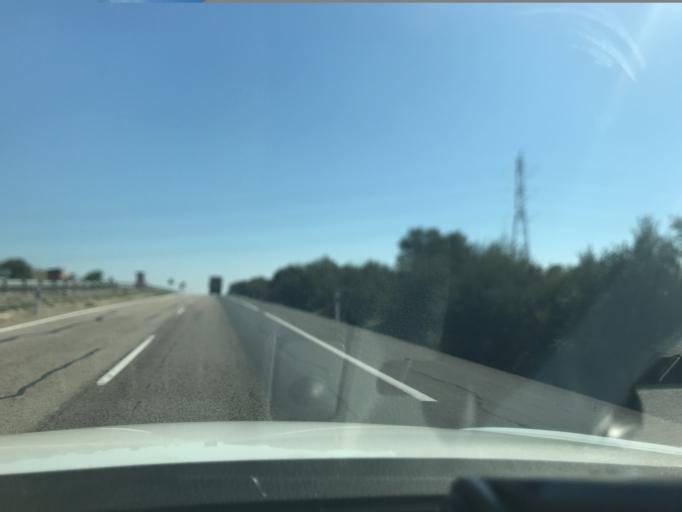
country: ES
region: Andalusia
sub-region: Provincia de Jaen
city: Lopera
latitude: 38.0069
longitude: -4.2233
